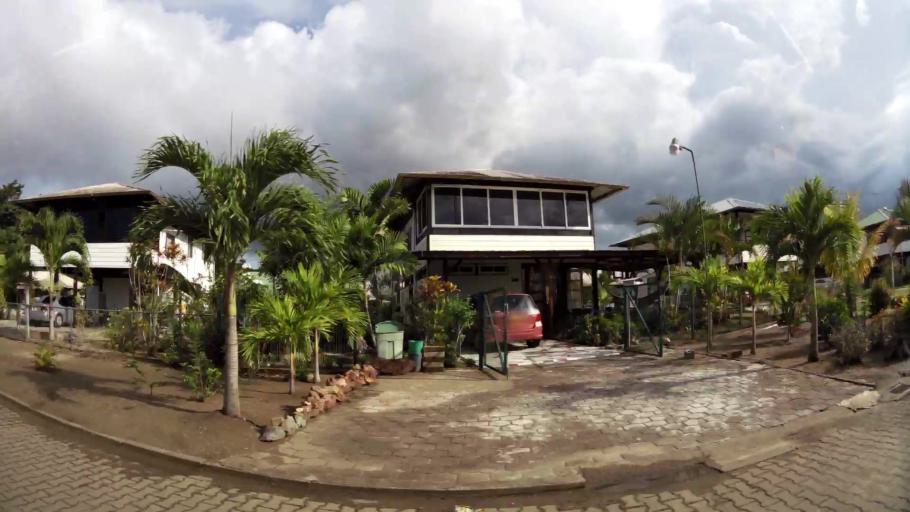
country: SR
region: Paramaribo
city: Paramaribo
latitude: 5.8462
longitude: -55.2115
